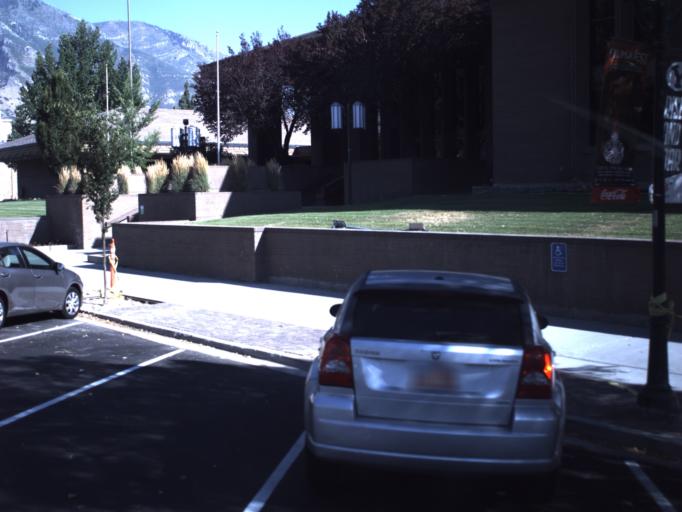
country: US
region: Utah
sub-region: Utah County
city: Provo
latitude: 40.2337
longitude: -111.6652
